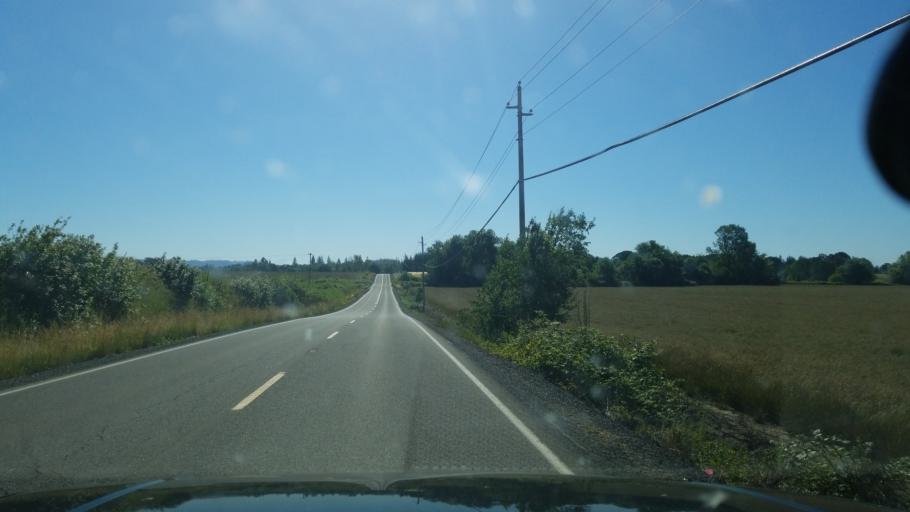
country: US
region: Oregon
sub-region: Yamhill County
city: McMinnville
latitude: 45.2305
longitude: -123.2403
